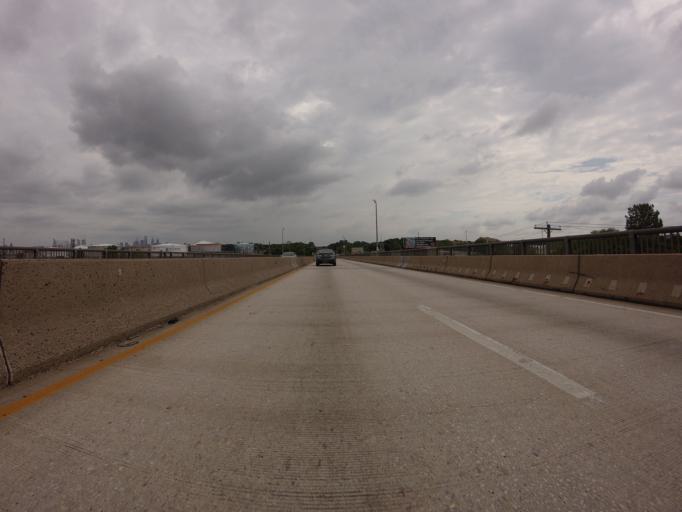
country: US
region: New Jersey
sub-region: Gloucester County
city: National Park
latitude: 39.9028
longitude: -75.2004
